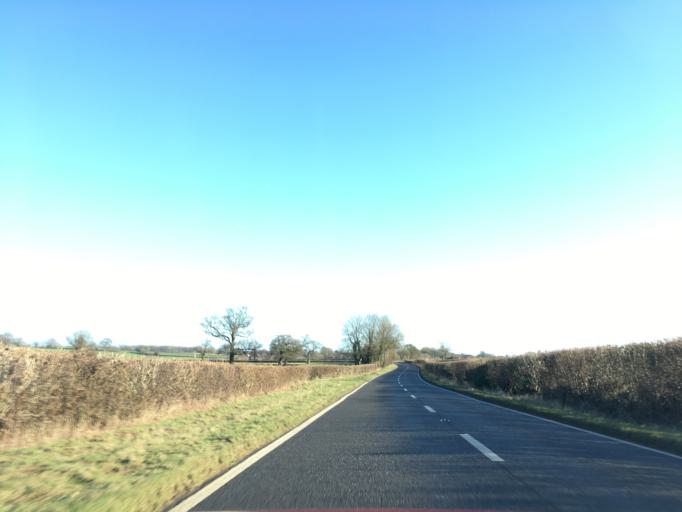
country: GB
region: England
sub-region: Wiltshire
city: Nettleton
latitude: 51.5270
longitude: -2.2929
